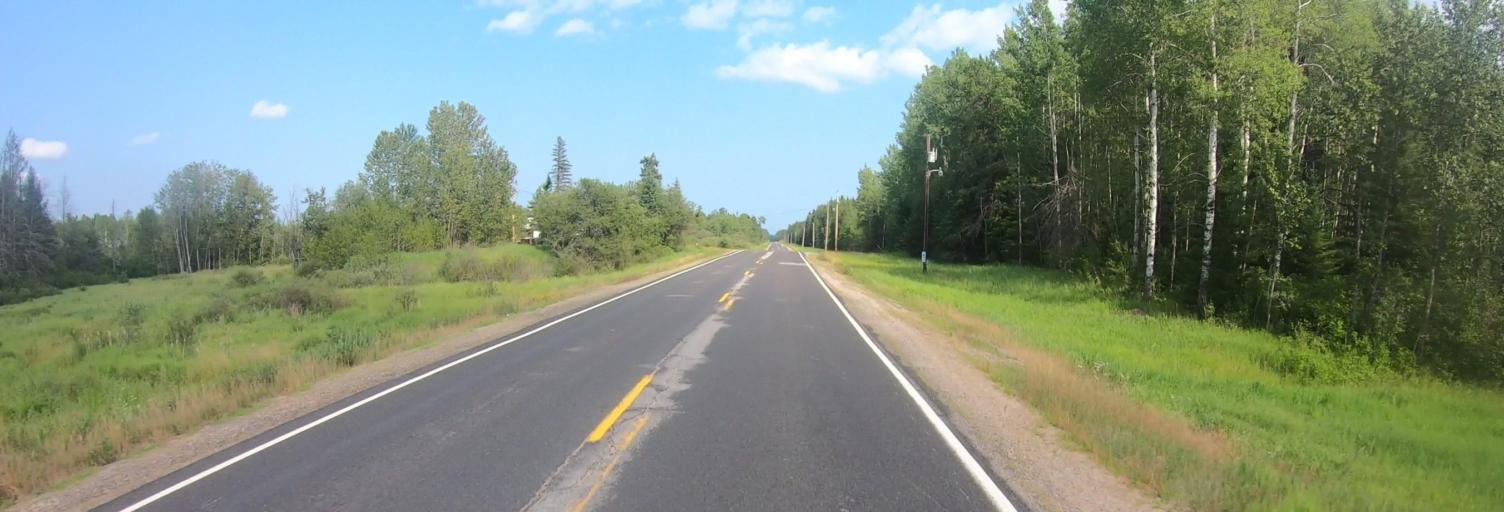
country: US
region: Minnesota
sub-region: Saint Louis County
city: Mountain Iron
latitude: 47.8914
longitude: -92.6732
